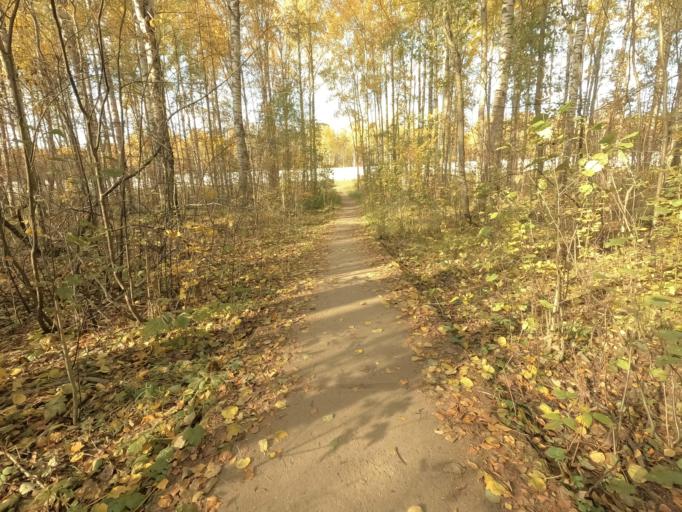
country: RU
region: Leningrad
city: Mga
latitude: 59.7590
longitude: 31.1145
